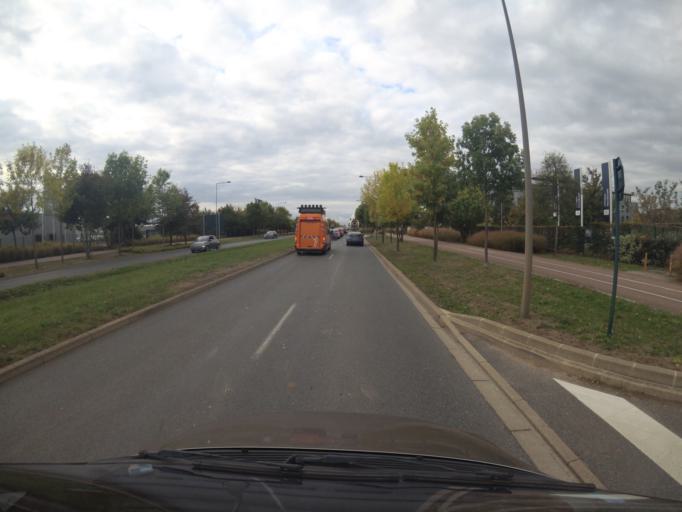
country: FR
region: Ile-de-France
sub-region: Departement de Seine-et-Marne
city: Chanteloup-en-Brie
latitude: 48.8533
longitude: 2.7609
